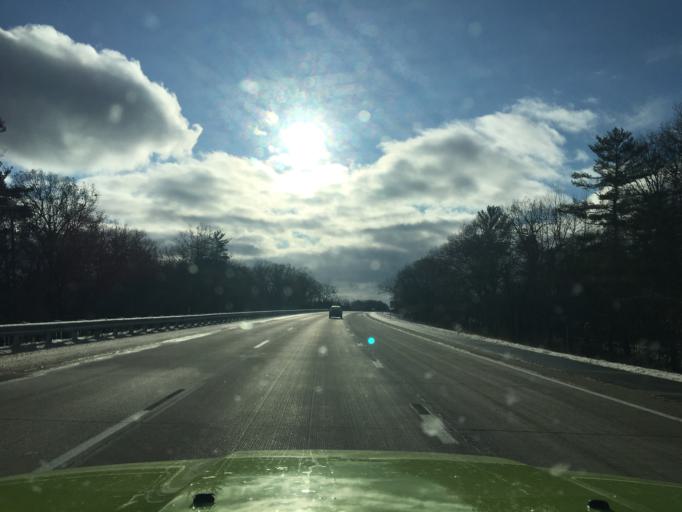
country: US
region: Michigan
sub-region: Kent County
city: Rockford
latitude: 43.1338
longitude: -85.5938
